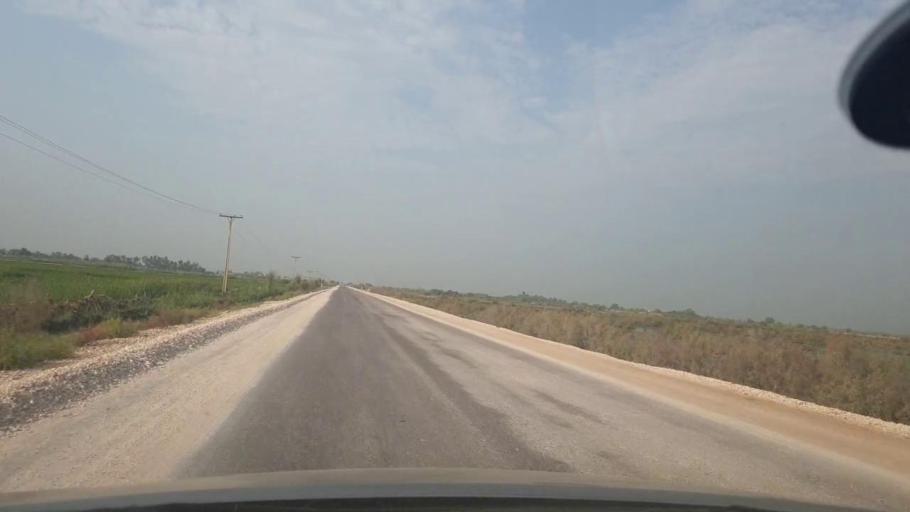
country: PK
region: Sindh
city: Jacobabad
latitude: 28.1451
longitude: 68.3458
